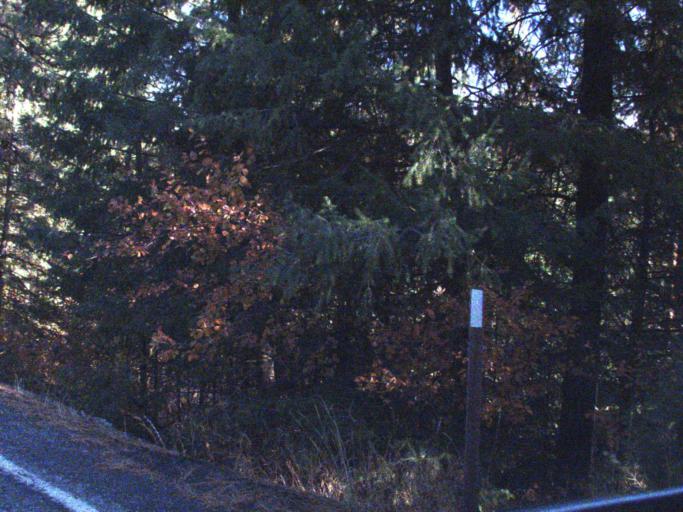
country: US
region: Washington
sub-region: Okanogan County
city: Coulee Dam
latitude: 48.0538
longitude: -118.6703
